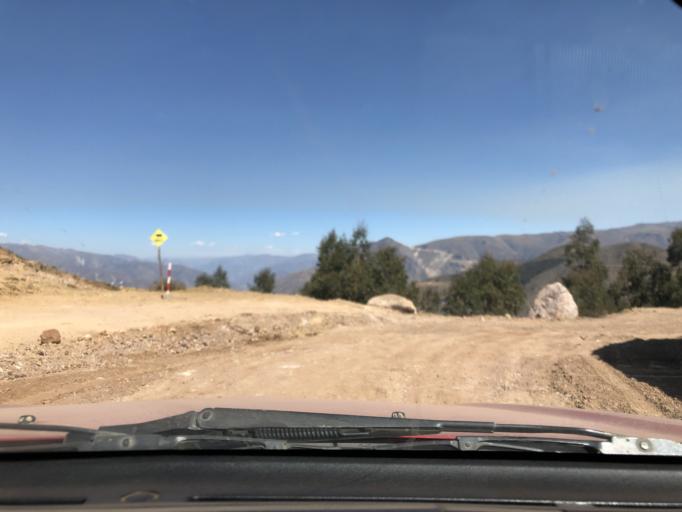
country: PE
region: Ayacucho
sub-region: Provincia de La Mar
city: Pampas
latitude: -13.1890
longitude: -73.8432
